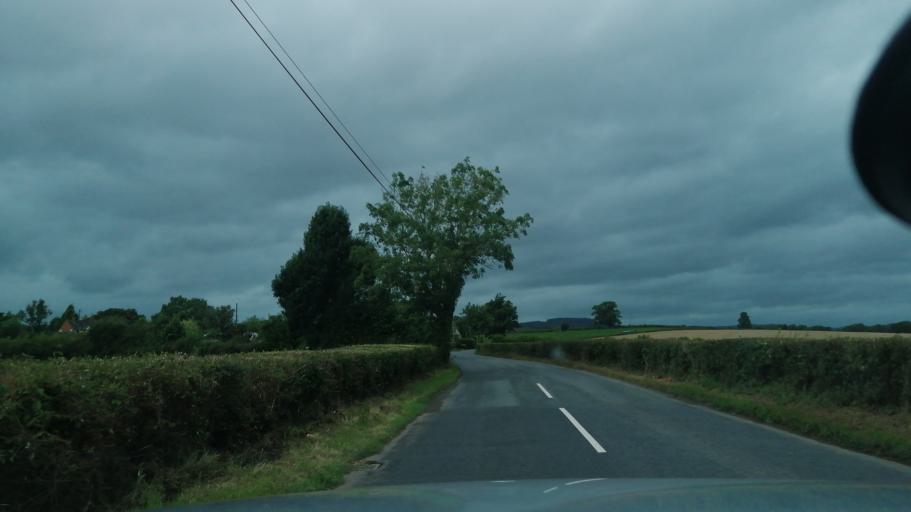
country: GB
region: England
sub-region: Herefordshire
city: Kingstone
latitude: 52.0093
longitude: -2.8269
